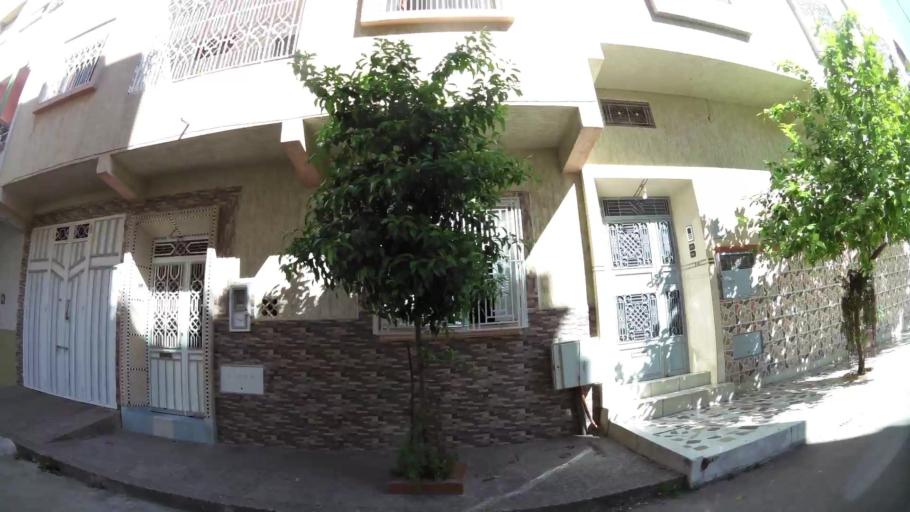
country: MA
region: Meknes-Tafilalet
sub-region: Meknes
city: Meknes
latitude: 33.8845
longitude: -5.5784
